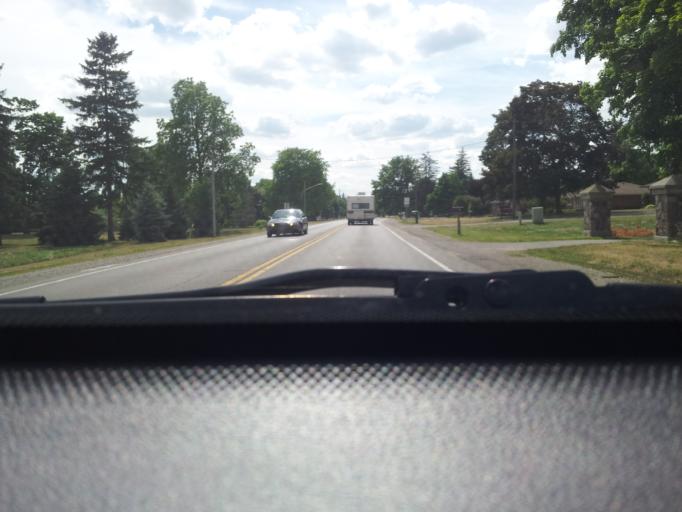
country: CA
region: Ontario
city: Brant
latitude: 43.1057
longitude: -80.4140
